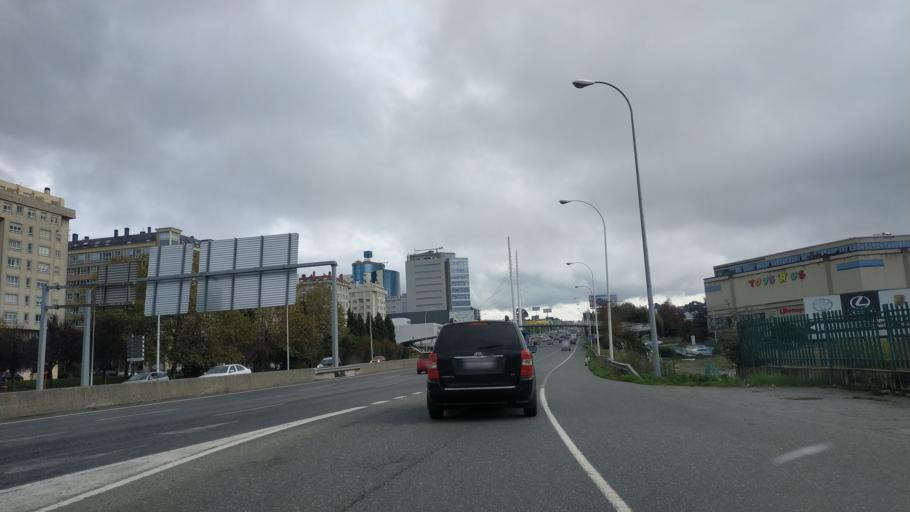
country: ES
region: Galicia
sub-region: Provincia da Coruna
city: A Coruna
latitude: 43.3422
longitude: -8.4084
